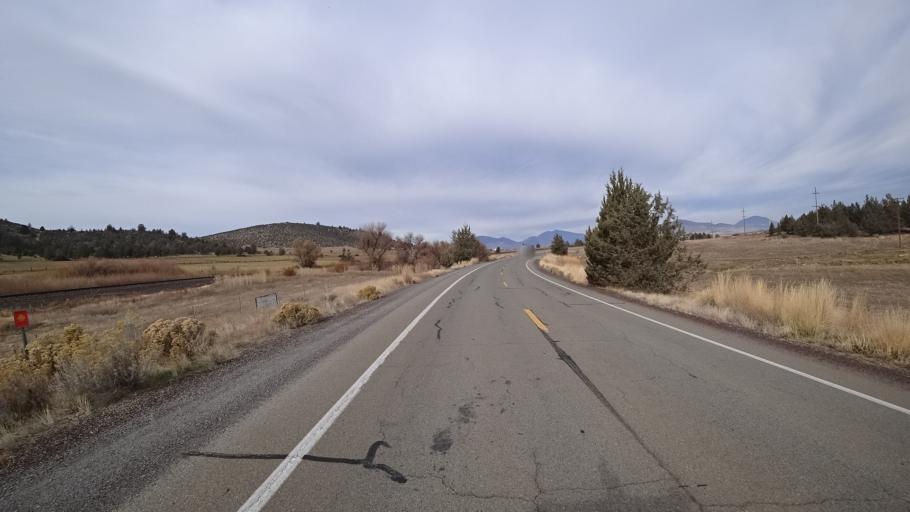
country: US
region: California
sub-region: Siskiyou County
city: Montague
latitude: 41.6847
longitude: -122.5345
